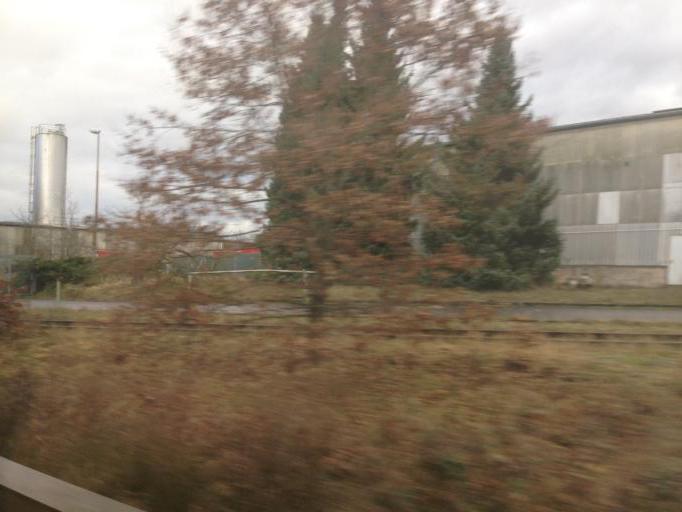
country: DE
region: Hesse
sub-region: Regierungsbezirk Giessen
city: Giessen
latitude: 50.5648
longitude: 8.6884
